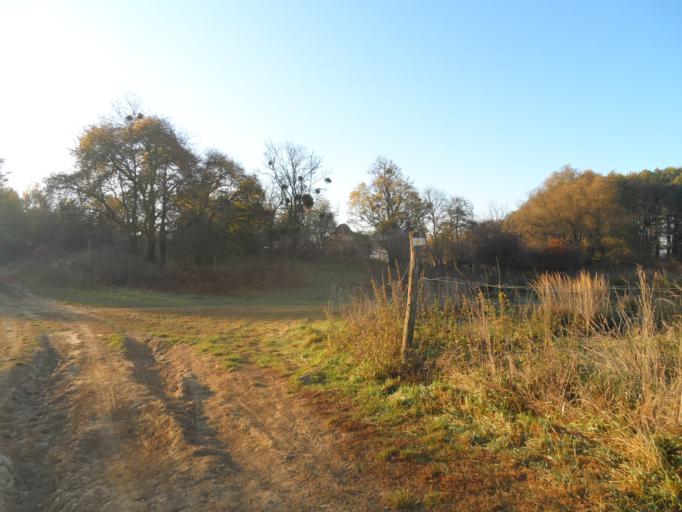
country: HU
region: Veszprem
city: Ajka
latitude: 47.1788
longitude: 17.5909
